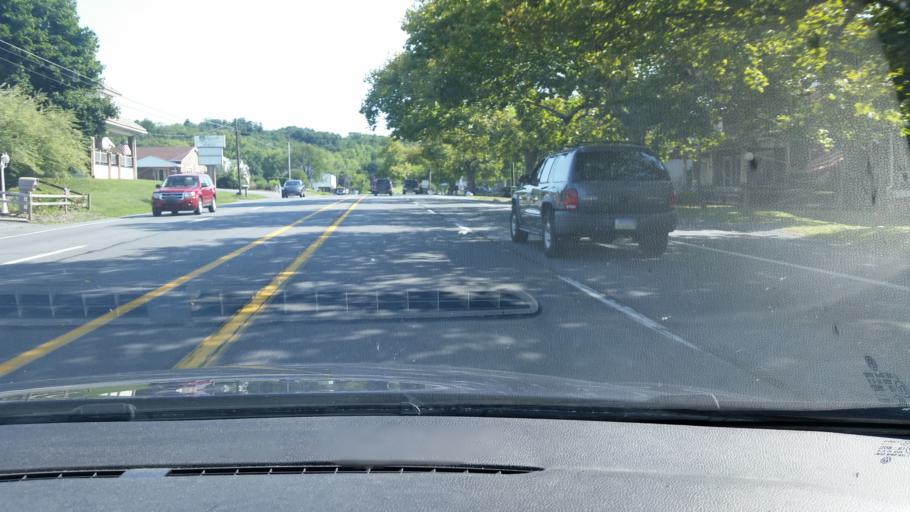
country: US
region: Pennsylvania
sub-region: Berks County
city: Hamburg
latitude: 40.5376
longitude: -75.9763
